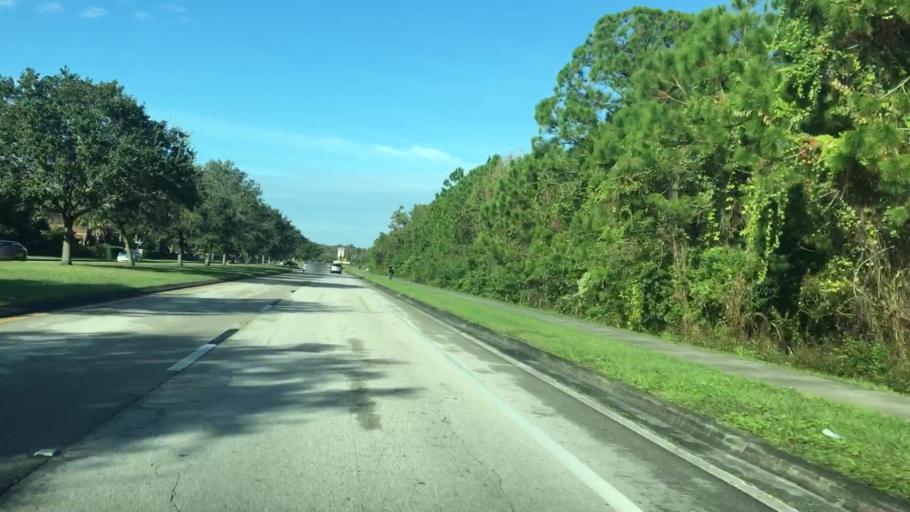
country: US
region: Florida
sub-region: Orange County
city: Azalea Park
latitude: 28.4786
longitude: -81.2506
